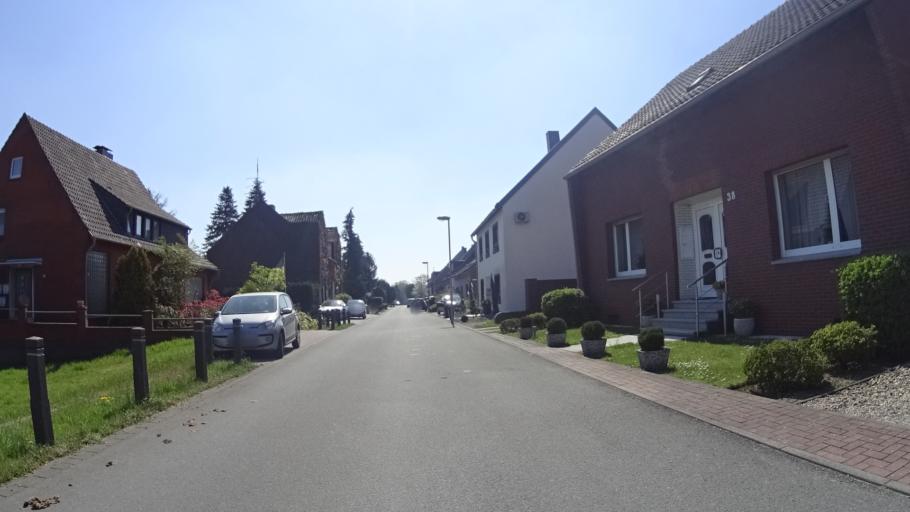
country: DE
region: North Rhine-Westphalia
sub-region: Regierungsbezirk Dusseldorf
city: Moers
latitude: 51.4225
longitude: 6.6187
